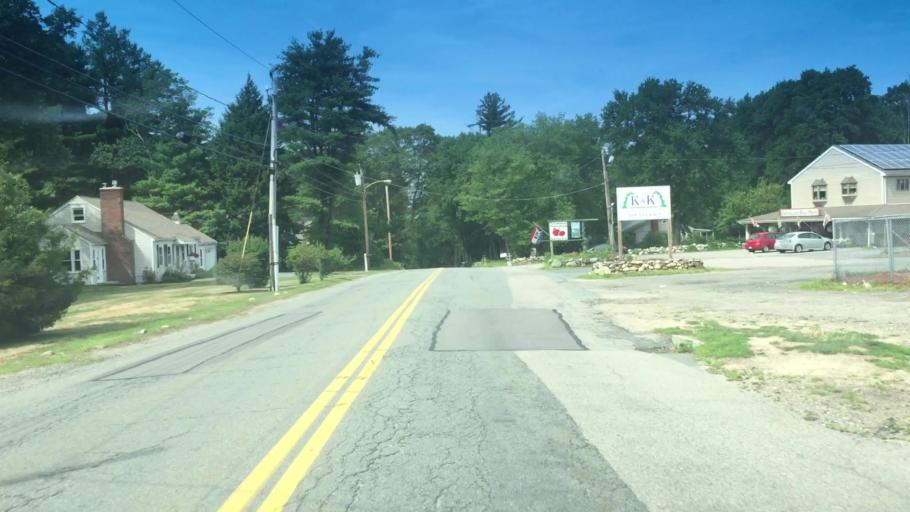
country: US
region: Massachusetts
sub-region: Norfolk County
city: Medway
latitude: 42.1349
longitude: -71.3997
